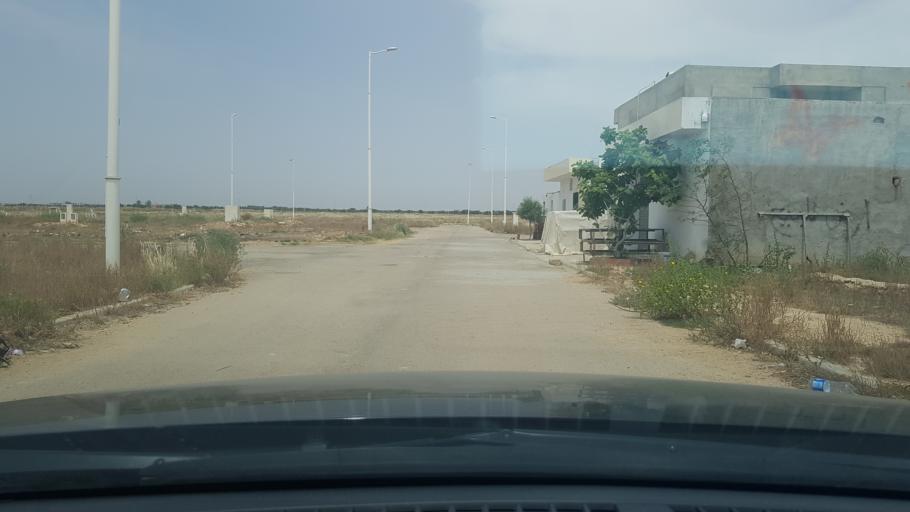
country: TN
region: Safaqis
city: Al Qarmadah
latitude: 34.8288
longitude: 10.7494
